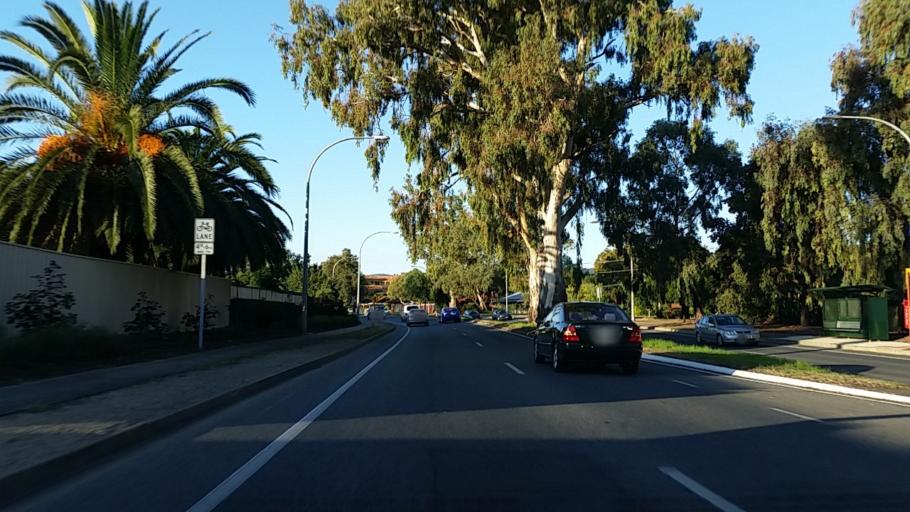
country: AU
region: South Australia
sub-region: Campbelltown
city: Paradise
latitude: -34.8670
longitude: 138.6776
